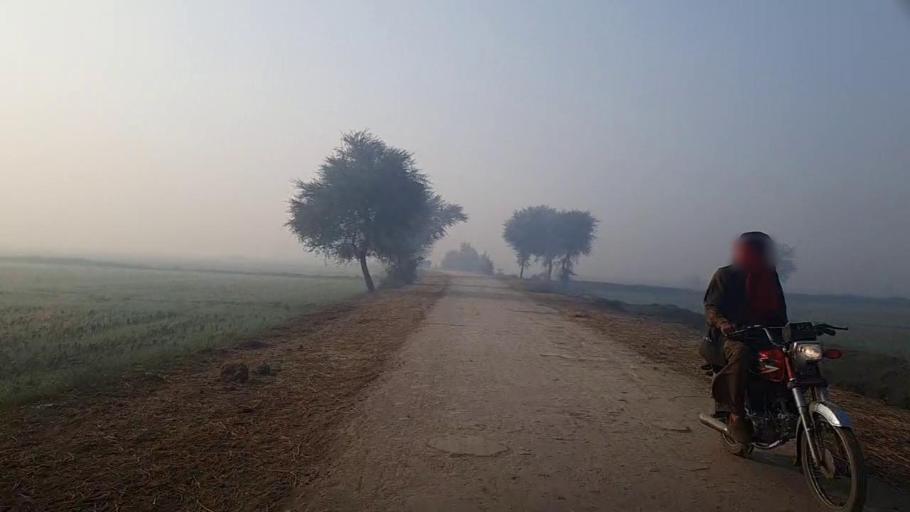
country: PK
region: Sindh
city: Mehar
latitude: 27.1619
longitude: 67.8244
